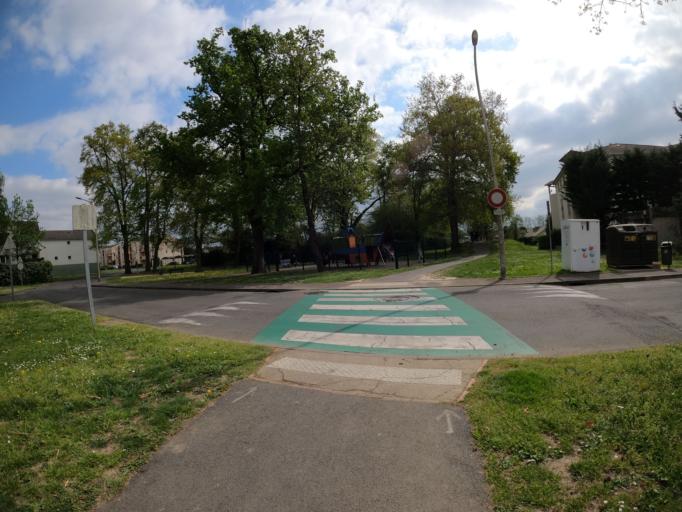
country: FR
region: Aquitaine
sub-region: Departement des Pyrenees-Atlantiques
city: Lons
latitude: 43.3222
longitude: -0.3848
